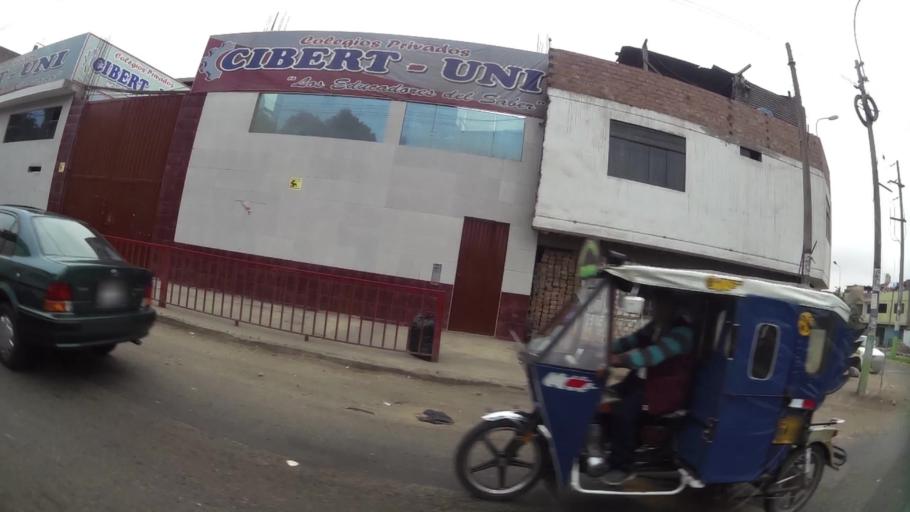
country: PE
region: Lima
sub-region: Lima
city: Vitarte
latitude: -12.0343
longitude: -76.9667
